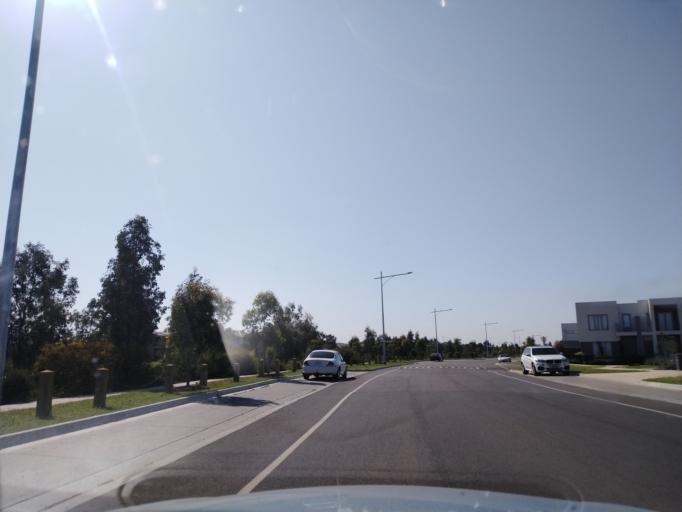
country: AU
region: Victoria
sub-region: Wyndham
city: Williams Landing
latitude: -37.8465
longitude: 144.7402
